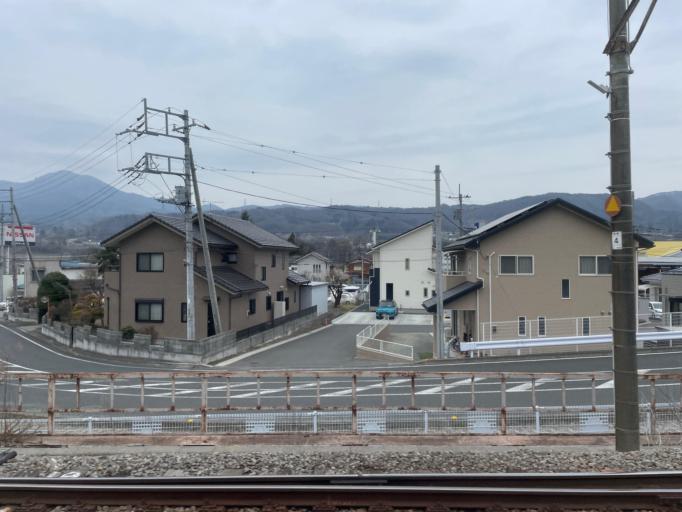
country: JP
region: Gunma
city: Numata
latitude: 36.6396
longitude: 139.0375
